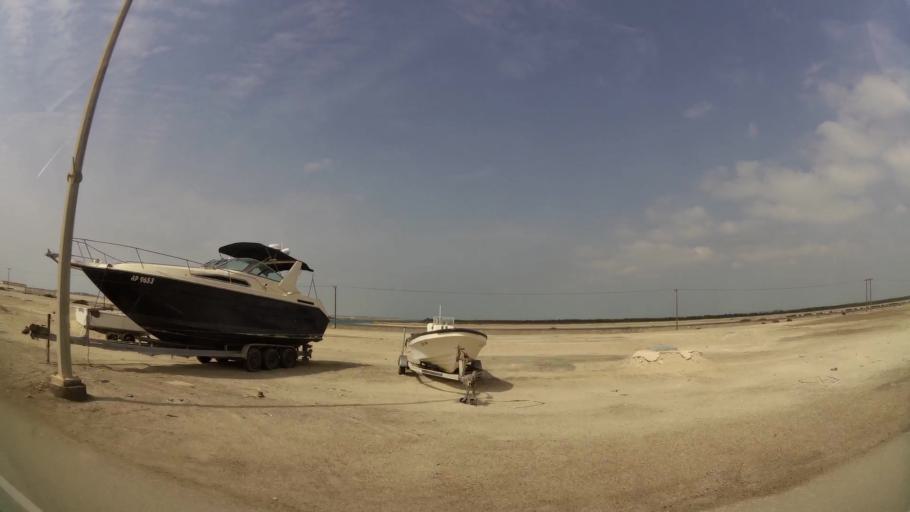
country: AE
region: Abu Dhabi
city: Abu Dhabi
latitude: 24.5625
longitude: 54.6375
